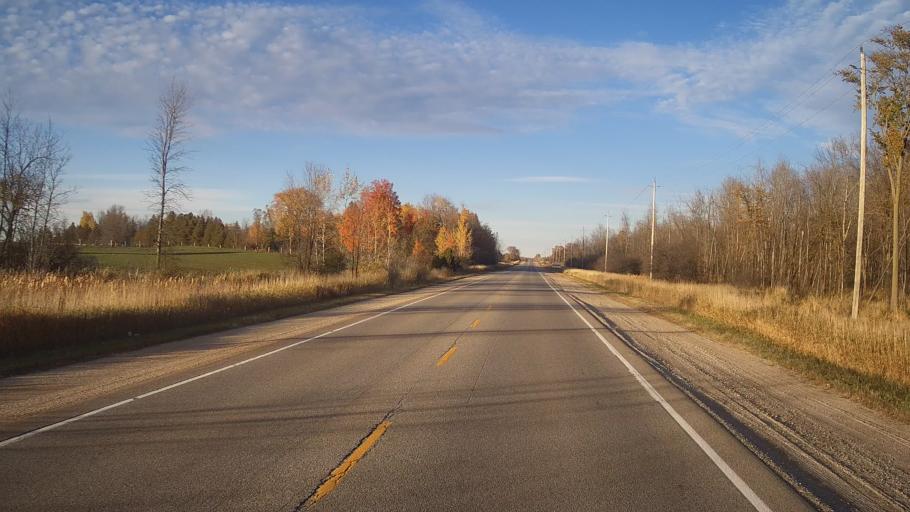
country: CA
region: Ontario
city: Perth
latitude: 44.9450
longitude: -76.2377
